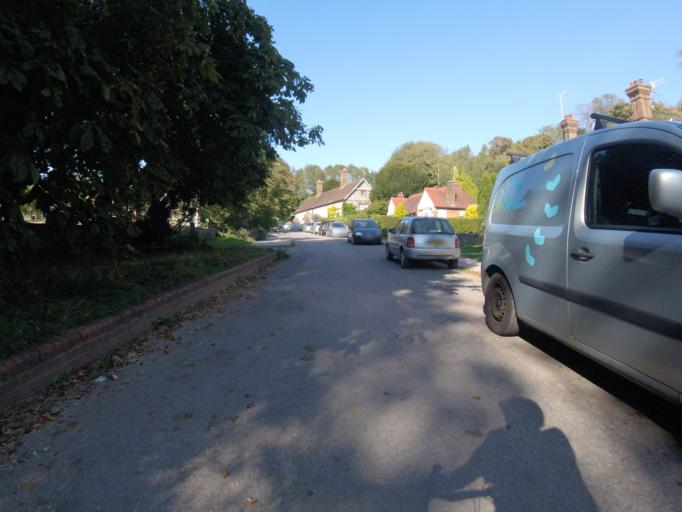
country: GB
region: England
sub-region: Brighton and Hove
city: Brighton
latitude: 50.8721
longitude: -0.1019
